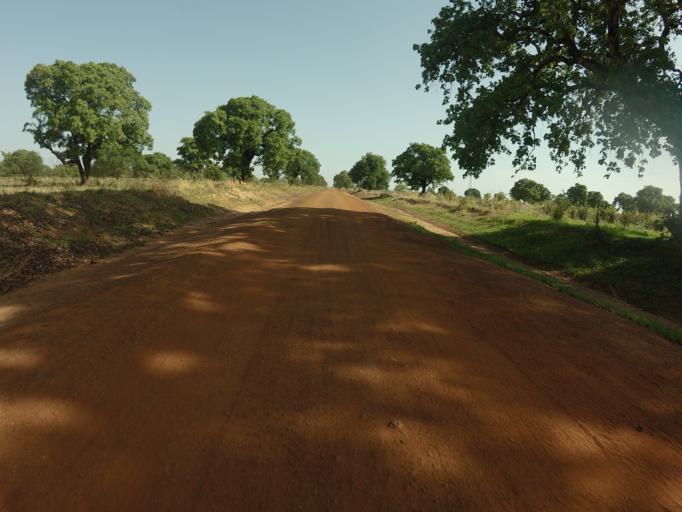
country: GH
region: Upper East
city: Bawku
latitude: 10.7715
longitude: -0.1944
